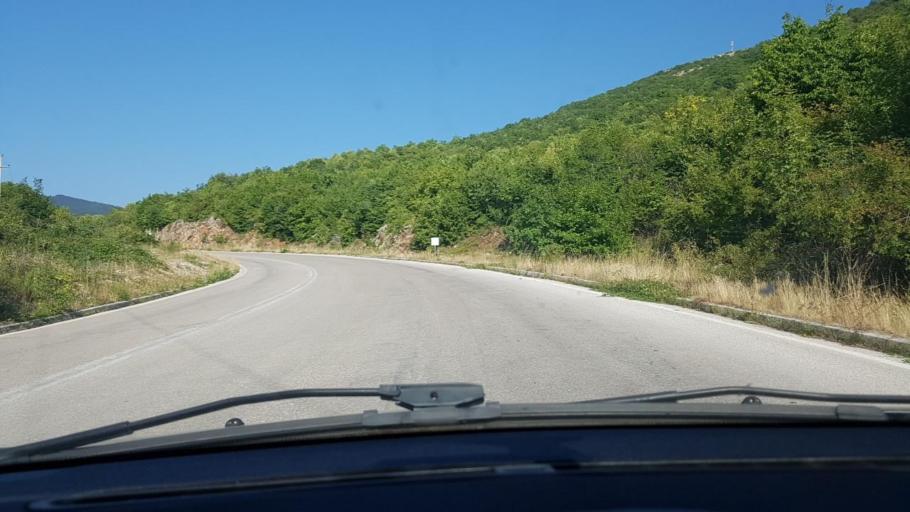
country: BA
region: Federation of Bosnia and Herzegovina
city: Rumboci
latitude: 43.8205
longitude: 17.4720
